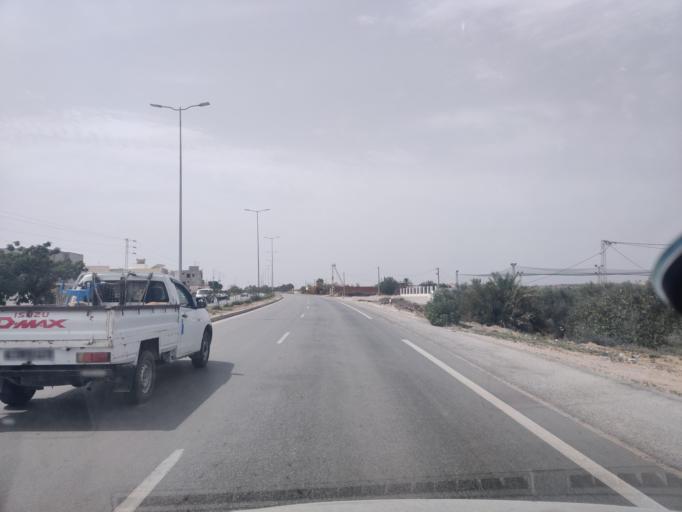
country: TN
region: Susah
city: Akouda
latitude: 35.8362
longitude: 10.5553
